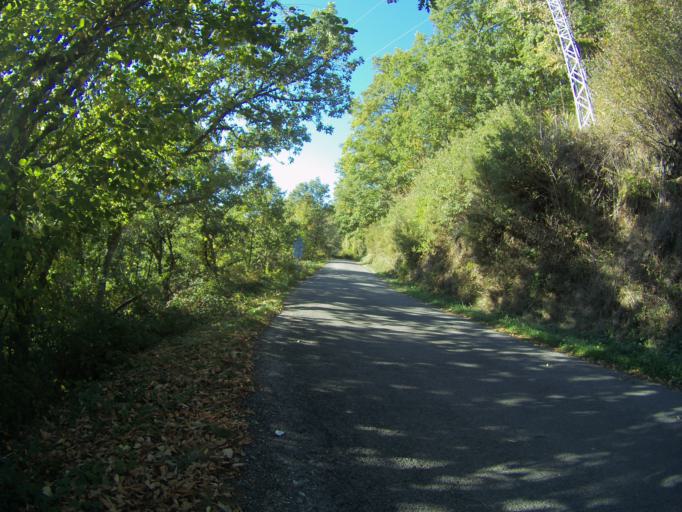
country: ES
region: Castille and Leon
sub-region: Provincia de Leon
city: Vega de Valcarce
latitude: 42.6834
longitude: -7.0021
